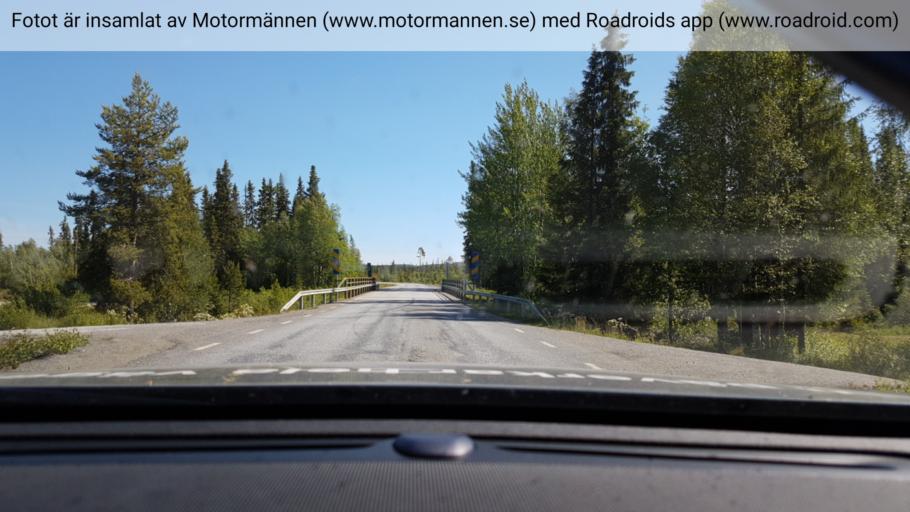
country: SE
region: Vaesterbotten
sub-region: Vilhelmina Kommun
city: Sjoberg
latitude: 64.7541
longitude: 16.1638
